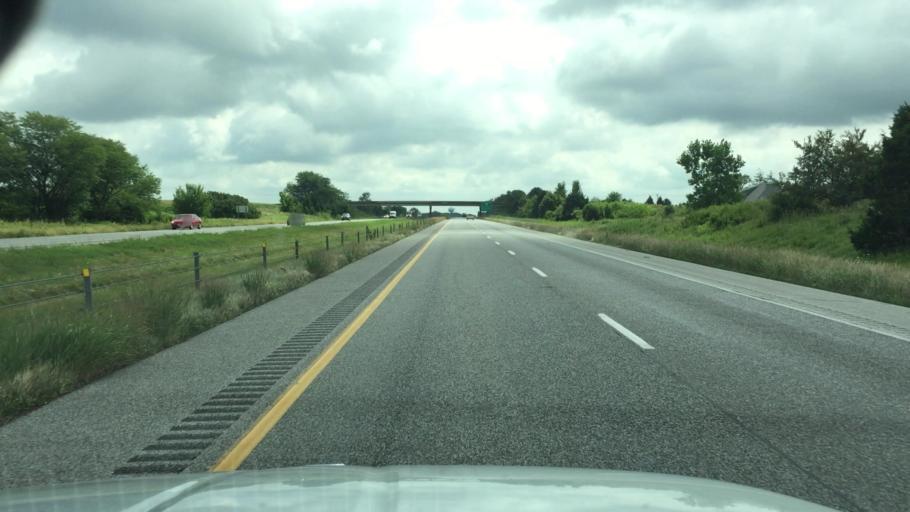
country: US
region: Illinois
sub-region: Rock Island County
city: Hampton
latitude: 41.5961
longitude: -90.3959
